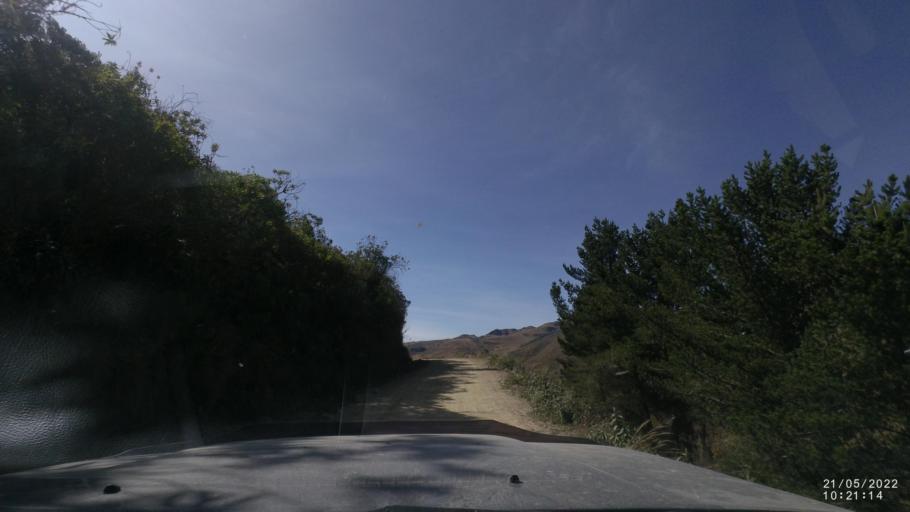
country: BO
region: Cochabamba
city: Colomi
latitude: -17.3269
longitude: -65.9584
